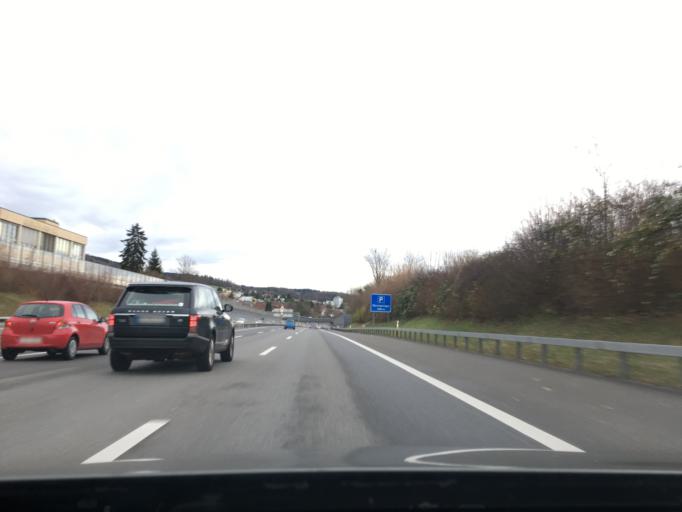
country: CH
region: Zurich
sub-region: Bezirk Dietikon
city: Schlieren / Engstingerquartier
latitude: 47.4102
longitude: 8.4411
